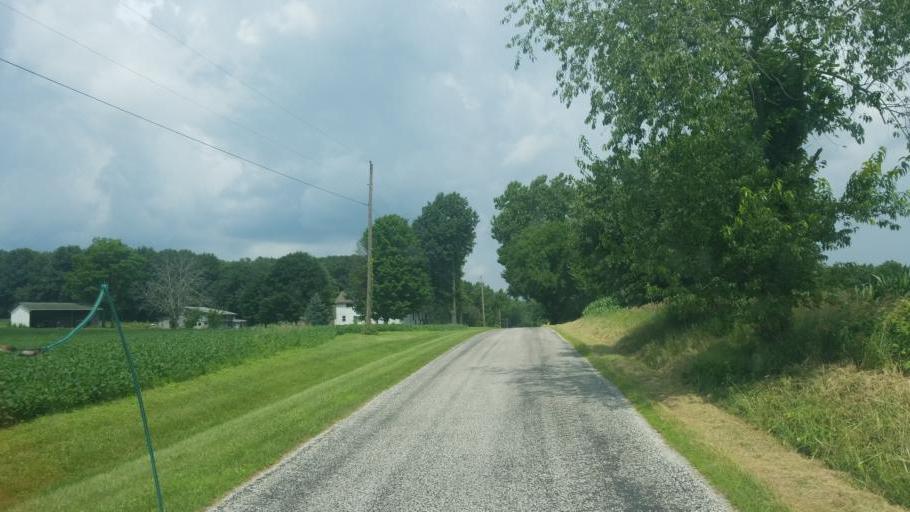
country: US
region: Ohio
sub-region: Wayne County
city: West Salem
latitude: 40.8258
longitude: -82.1416
